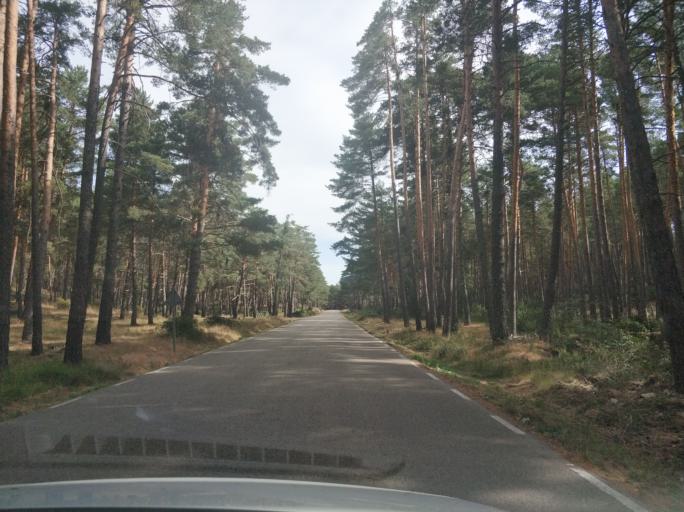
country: ES
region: Castille and Leon
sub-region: Provincia de Soria
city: Navaleno
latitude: 41.8441
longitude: -2.9933
